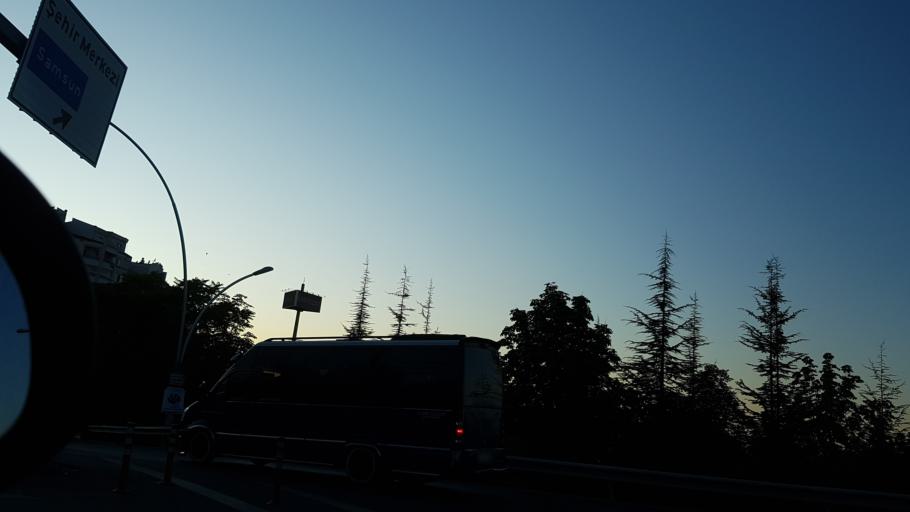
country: TR
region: Ankara
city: Batikent
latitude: 39.9046
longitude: 32.7106
